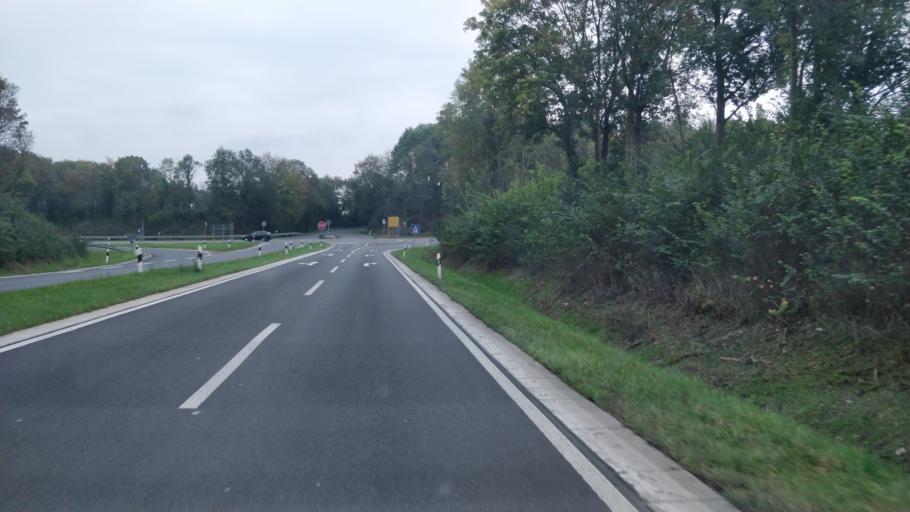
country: DE
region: North Rhine-Westphalia
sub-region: Regierungsbezirk Koln
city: Weilerswist
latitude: 50.7159
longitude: 6.8960
